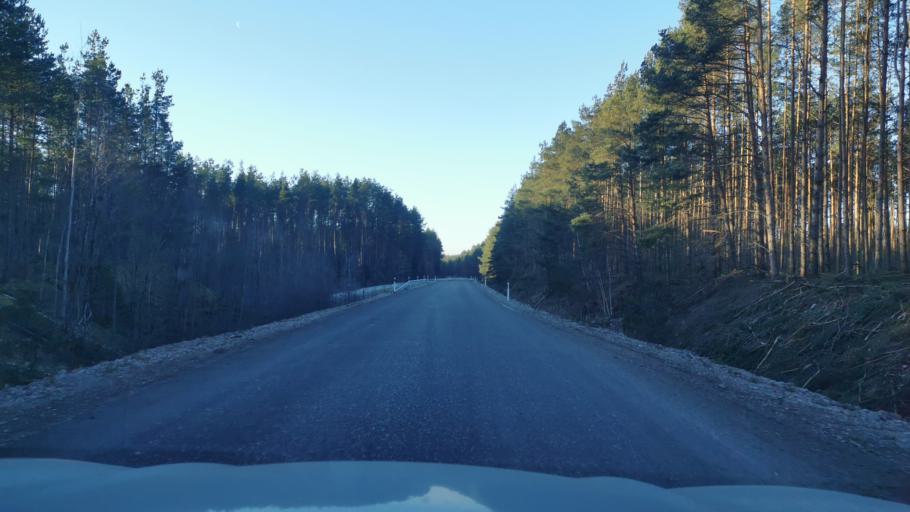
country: EE
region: Ida-Virumaa
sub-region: Kohtla-Nomme vald
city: Kohtla-Nomme
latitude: 59.3388
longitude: 27.1283
